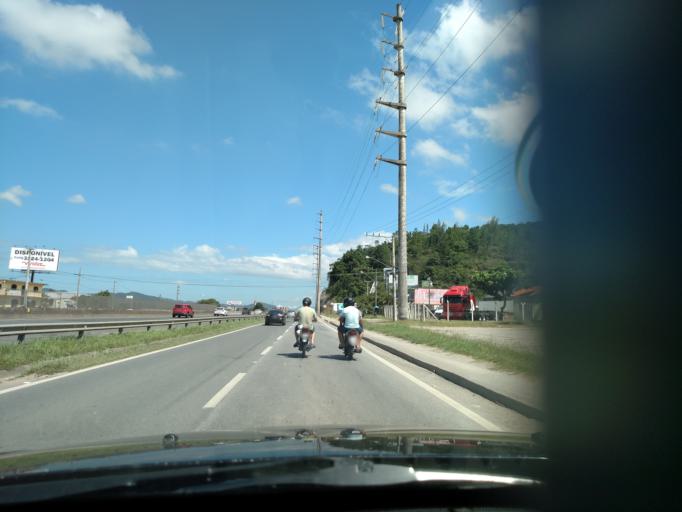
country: BR
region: Santa Catarina
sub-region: Itajai
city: Itajai
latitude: -26.8946
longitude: -48.7197
